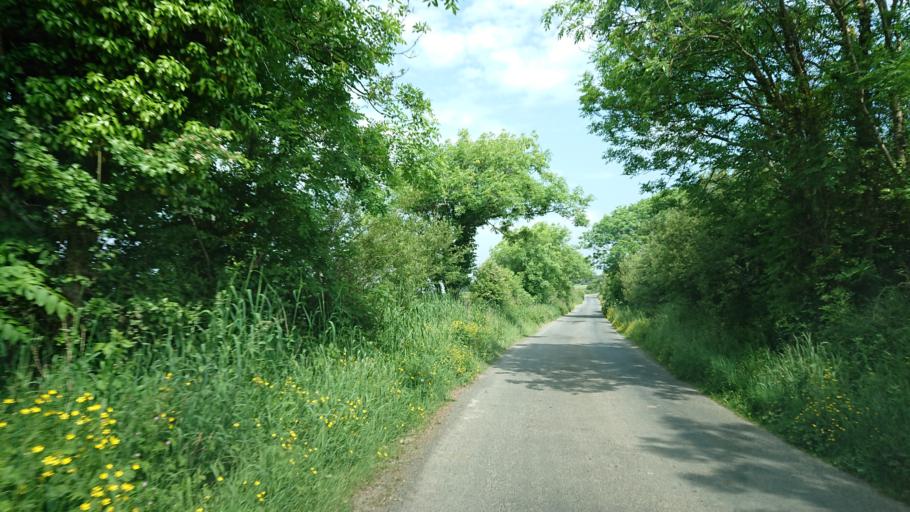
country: IE
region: Munster
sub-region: Waterford
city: Dunmore East
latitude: 52.2245
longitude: -7.0059
